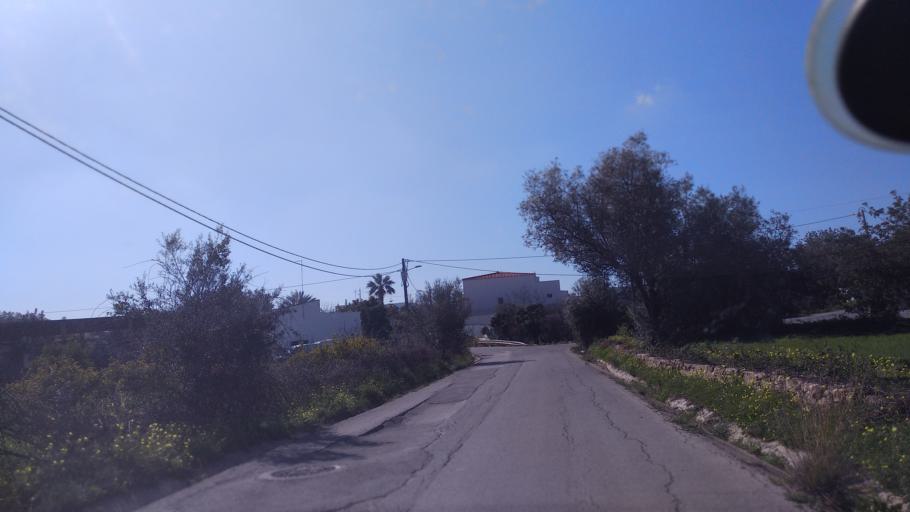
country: PT
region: Faro
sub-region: Sao Bras de Alportel
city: Sao Bras de Alportel
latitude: 37.1265
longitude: -7.9210
